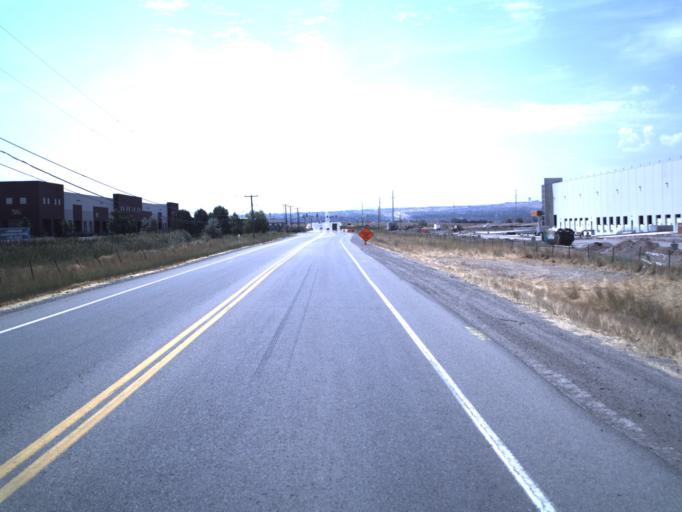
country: US
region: Utah
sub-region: Salt Lake County
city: West Valley City
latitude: 40.7358
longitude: -112.0249
